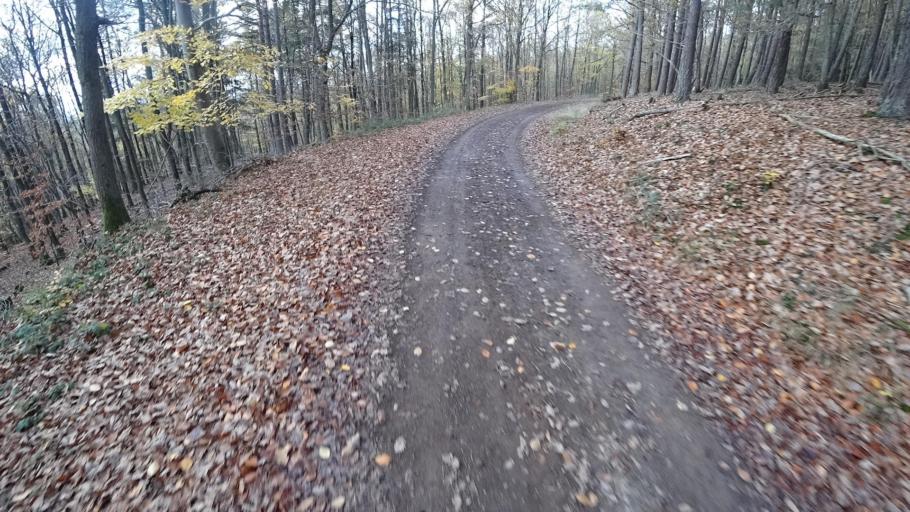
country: DE
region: Rheinland-Pfalz
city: Lind
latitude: 50.4806
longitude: 6.9356
